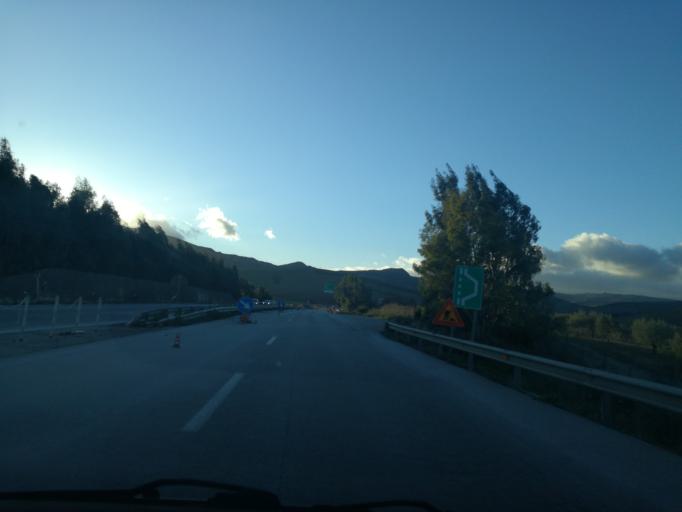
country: IT
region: Sicily
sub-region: Palermo
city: Castellana Sicula
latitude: 37.7439
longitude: 13.9833
